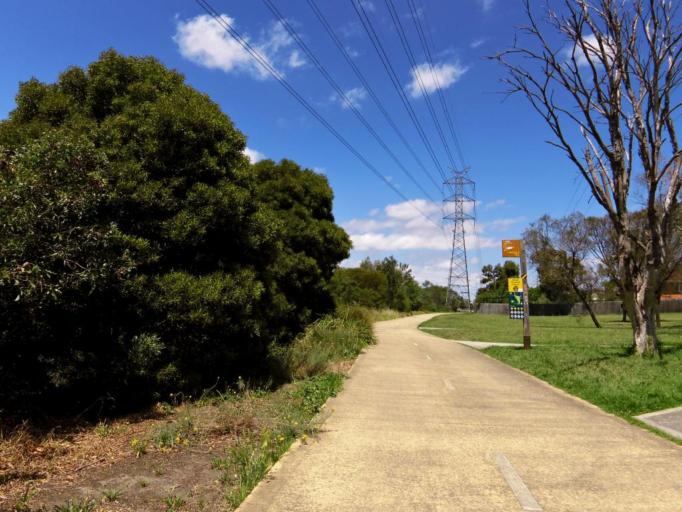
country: AU
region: Victoria
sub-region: Moreland
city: Coburg
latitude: -37.7580
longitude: 144.9802
